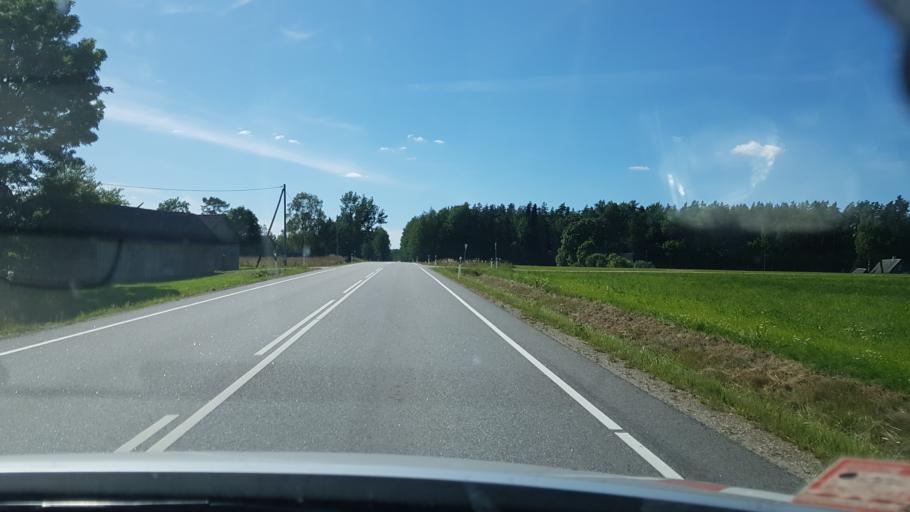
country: EE
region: Polvamaa
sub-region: Polva linn
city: Polva
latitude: 58.0617
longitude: 26.9537
